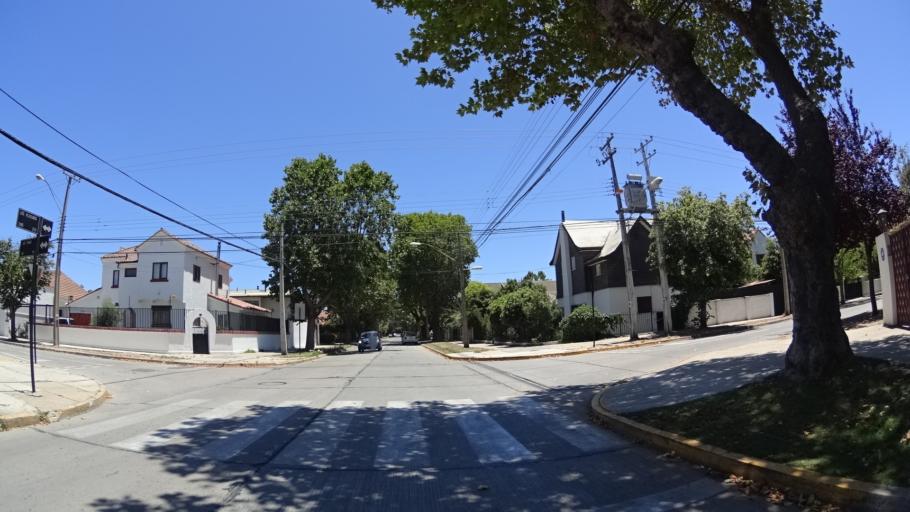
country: CL
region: Valparaiso
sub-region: Provincia de Valparaiso
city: Vina del Mar
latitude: -33.0292
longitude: -71.5320
